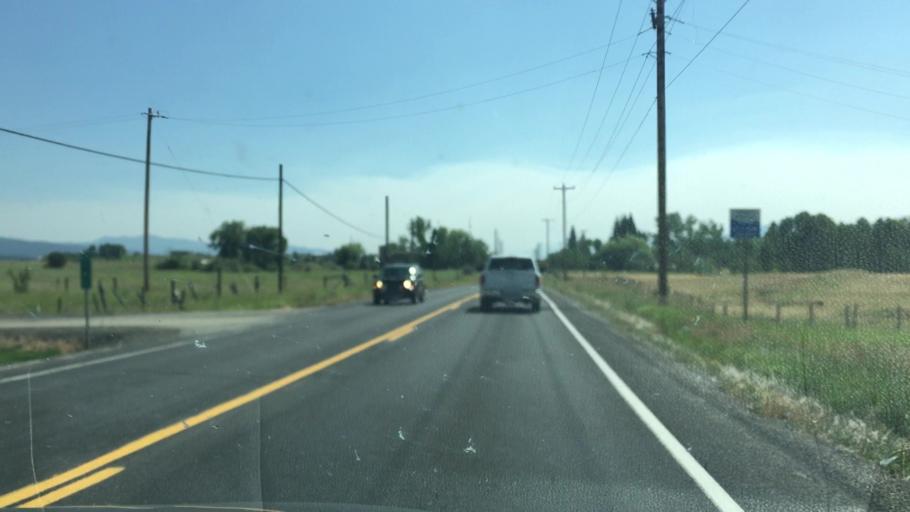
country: US
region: Idaho
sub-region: Valley County
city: McCall
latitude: 44.8690
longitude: -116.0908
